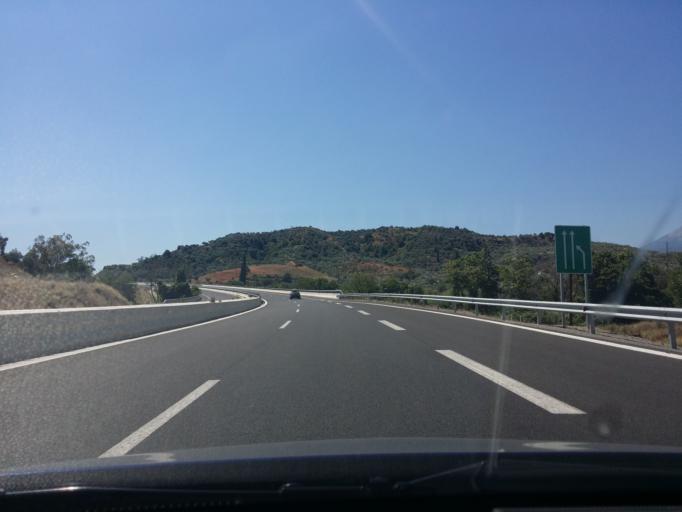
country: GR
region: Peloponnese
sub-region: Nomos Lakonias
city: Magoula
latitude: 37.1317
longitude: 22.3994
